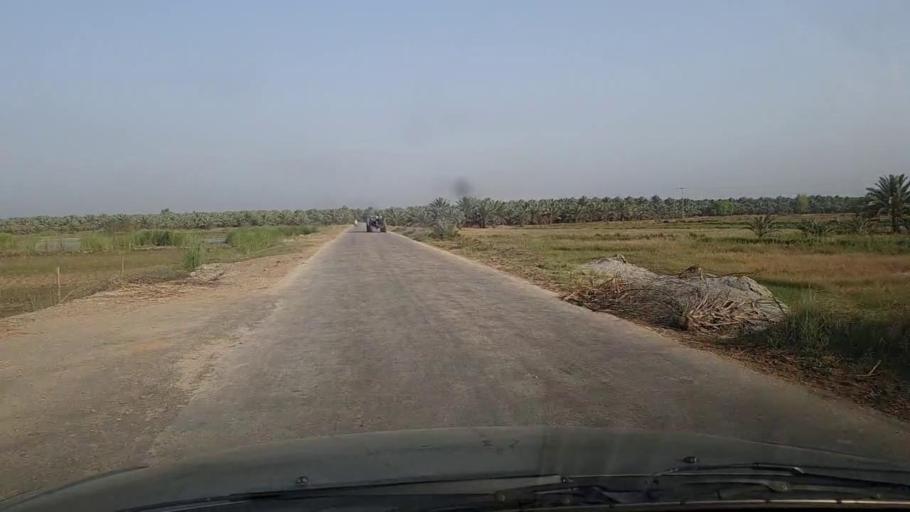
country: PK
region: Sindh
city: Pir jo Goth
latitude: 27.5654
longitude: 68.6439
